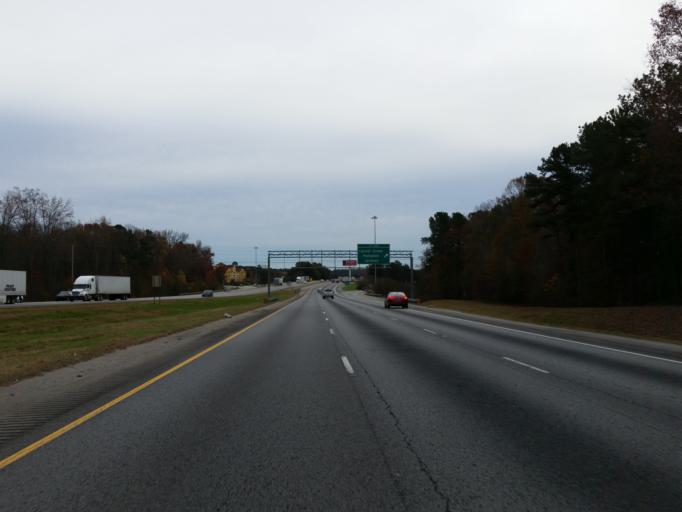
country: US
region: Georgia
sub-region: Henry County
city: Locust Grove
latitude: 33.3579
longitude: -84.1277
